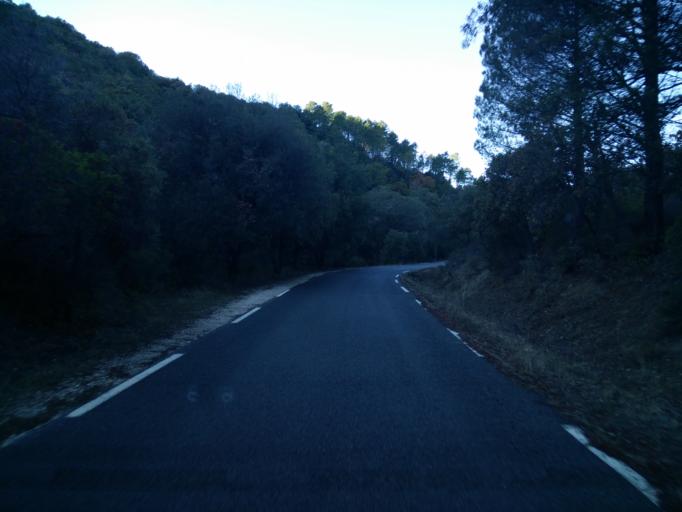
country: FR
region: Provence-Alpes-Cote d'Azur
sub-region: Departement du Var
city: Collobrieres
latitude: 43.2348
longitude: 6.3611
